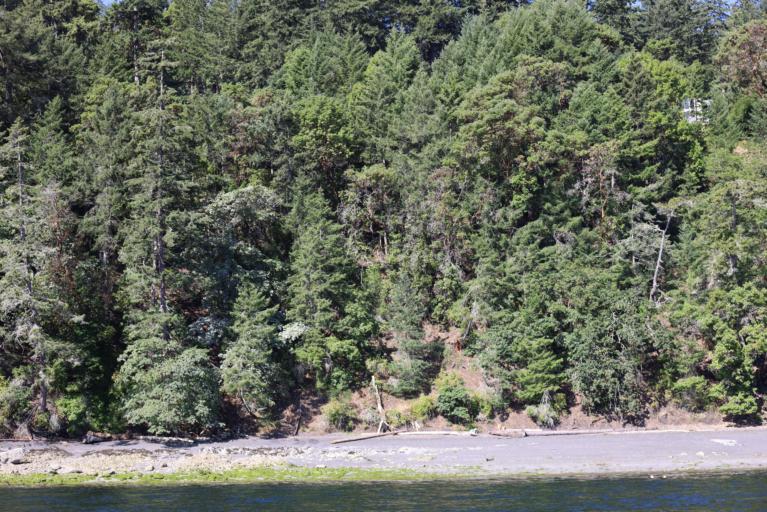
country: CA
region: British Columbia
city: North Cowichan
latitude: 48.8102
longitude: -123.6056
